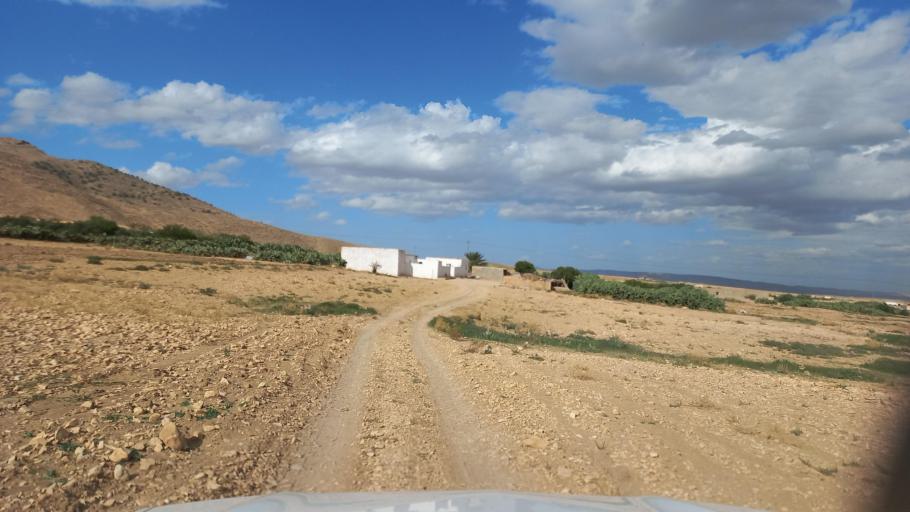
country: TN
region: Al Qasrayn
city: Sbiba
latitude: 35.4501
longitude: 9.0697
